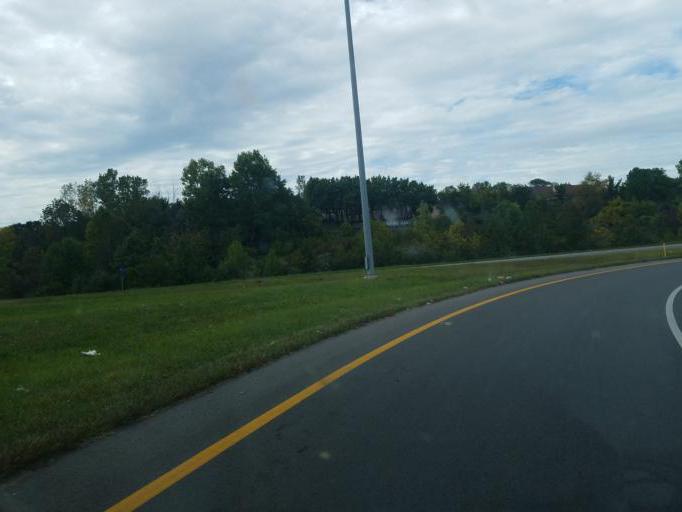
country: US
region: Ohio
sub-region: Franklin County
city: Reynoldsburg
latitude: 39.9552
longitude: -82.8463
